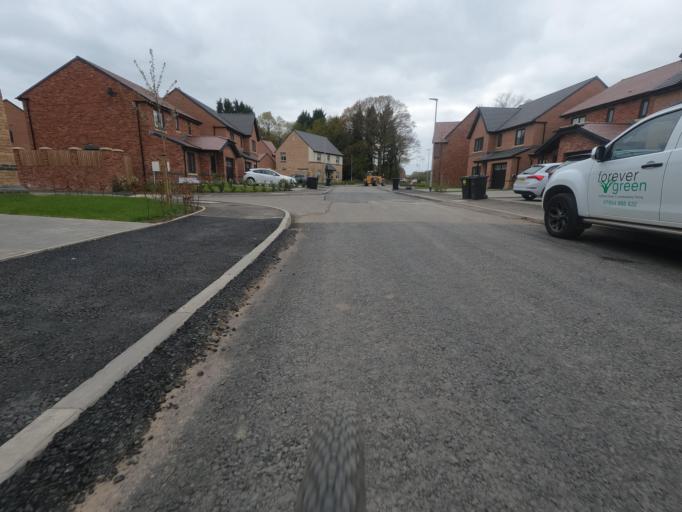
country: GB
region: England
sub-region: Northumberland
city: Ponteland
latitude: 55.0603
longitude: -1.7627
